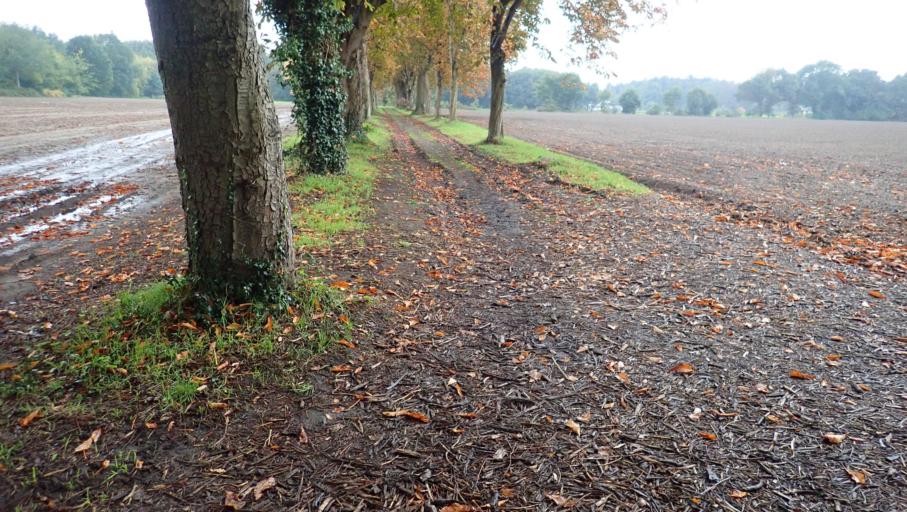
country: BE
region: Flanders
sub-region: Provincie Antwerpen
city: Nijlen
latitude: 51.1456
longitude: 4.6751
